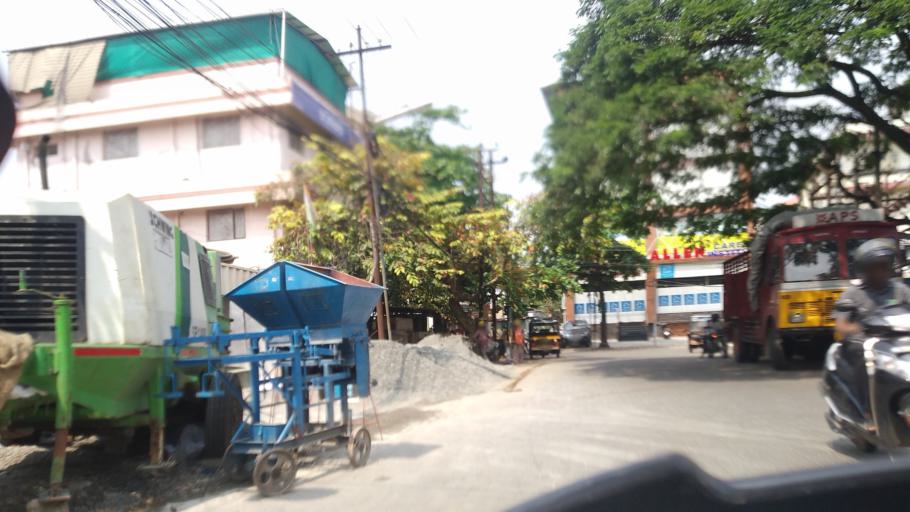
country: IN
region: Kerala
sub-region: Ernakulam
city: Cochin
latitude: 9.9749
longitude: 76.2830
